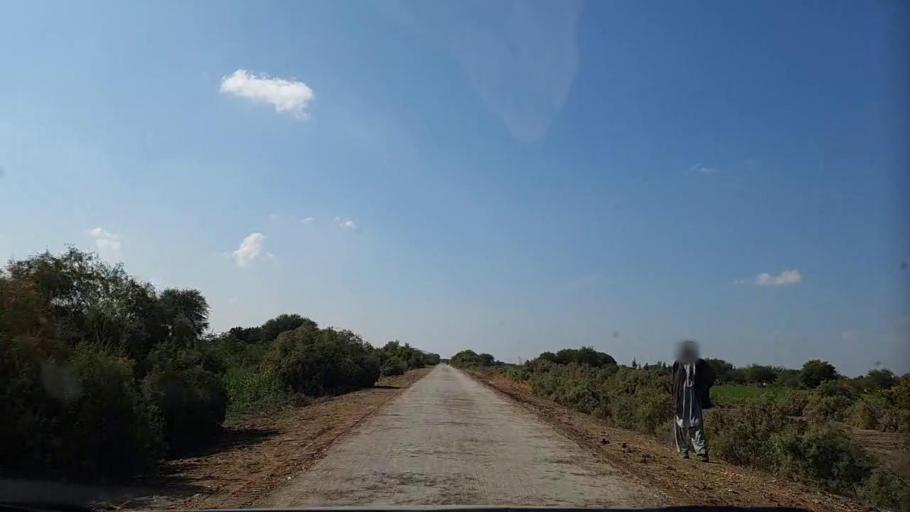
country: PK
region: Sindh
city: Pithoro
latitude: 25.6688
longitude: 69.4705
